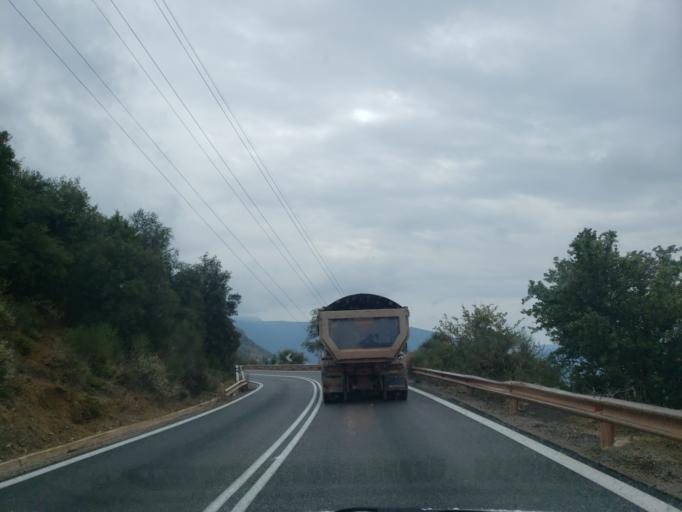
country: GR
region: Central Greece
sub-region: Nomos Fokidos
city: Amfissa
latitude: 38.5666
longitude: 22.3993
